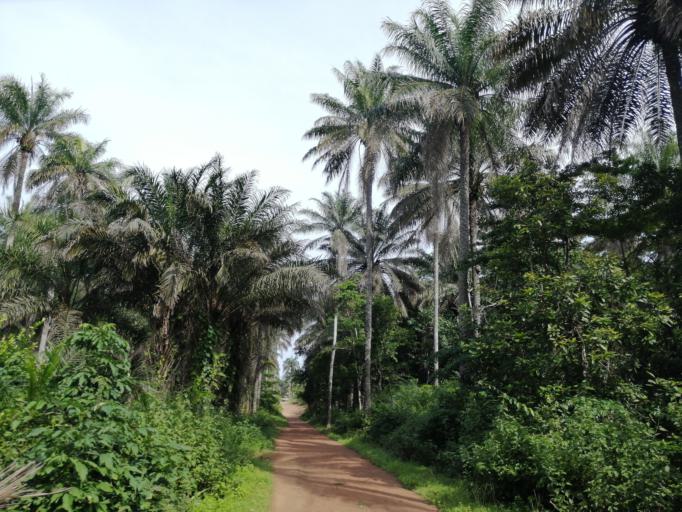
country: SL
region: Northern Province
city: Port Loko
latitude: 8.7899
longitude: -12.9298
